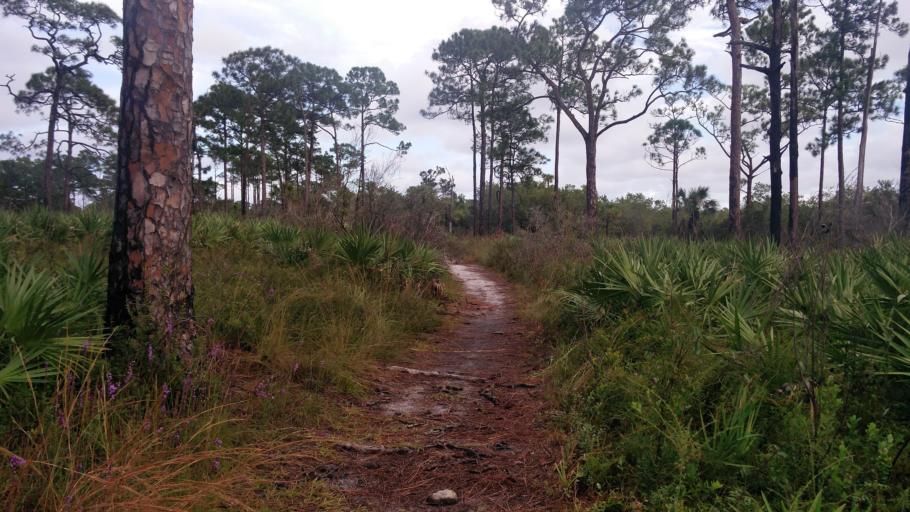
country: US
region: Florida
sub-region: Palm Beach County
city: Tequesta
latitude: 26.9921
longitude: -80.1501
